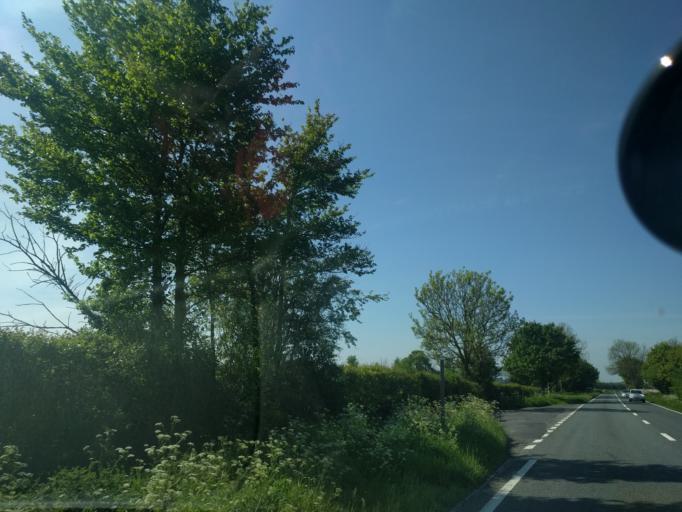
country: GB
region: England
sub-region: Somerset
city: Castle Cary
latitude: 51.1212
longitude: -2.5758
